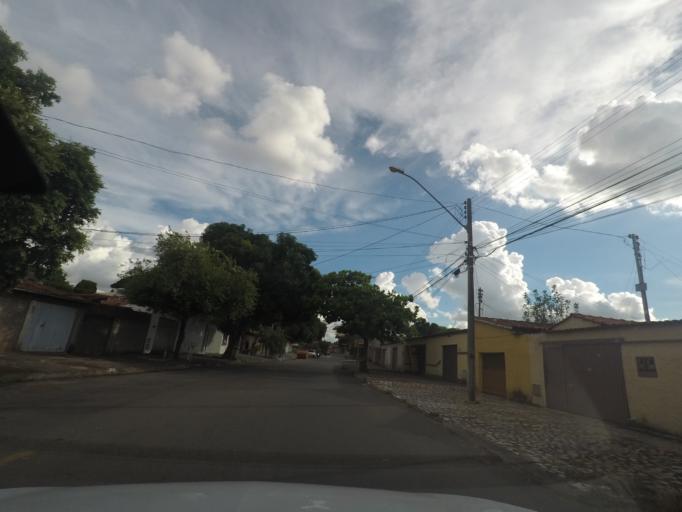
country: BR
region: Goias
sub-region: Goiania
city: Goiania
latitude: -16.7139
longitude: -49.3040
